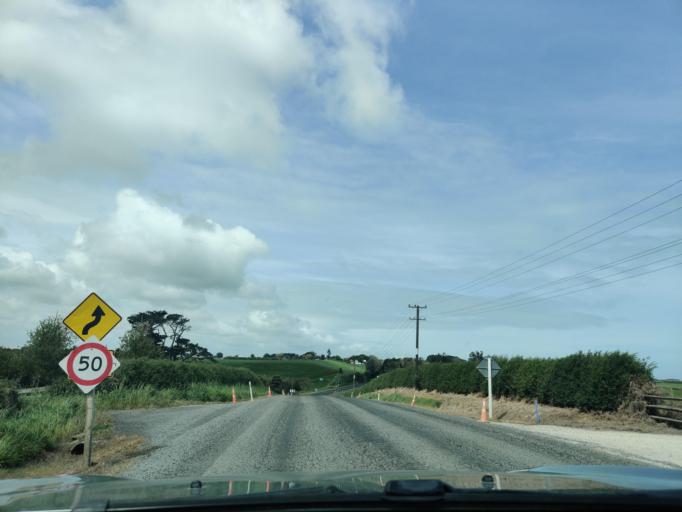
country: NZ
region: Taranaki
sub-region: South Taranaki District
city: Hawera
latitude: -39.5857
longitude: 174.2480
